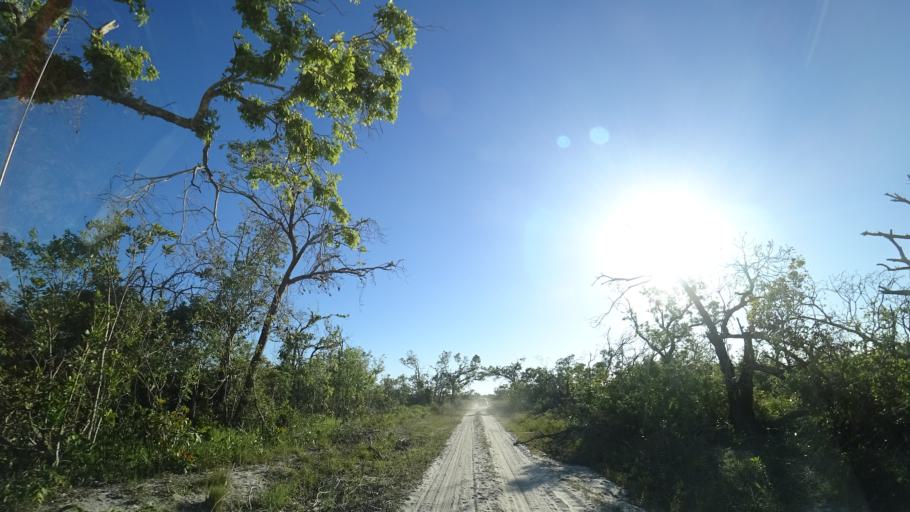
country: MZ
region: Sofala
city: Beira
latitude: -19.5756
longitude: 35.2101
